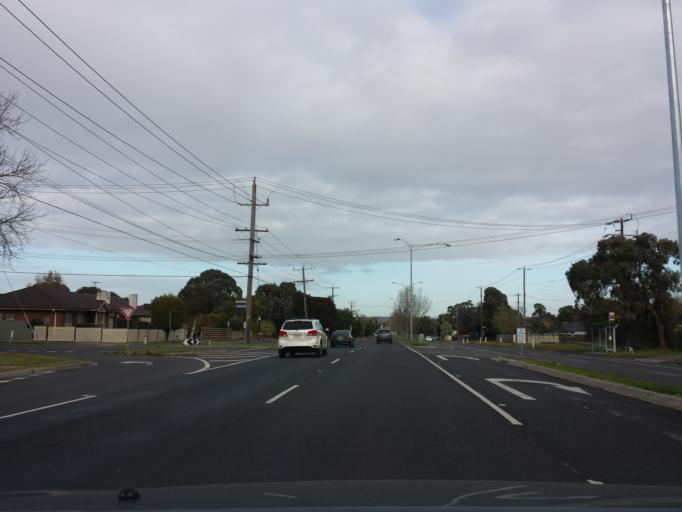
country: AU
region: Victoria
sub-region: Knox
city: Knoxfield
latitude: -37.8858
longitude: 145.2671
